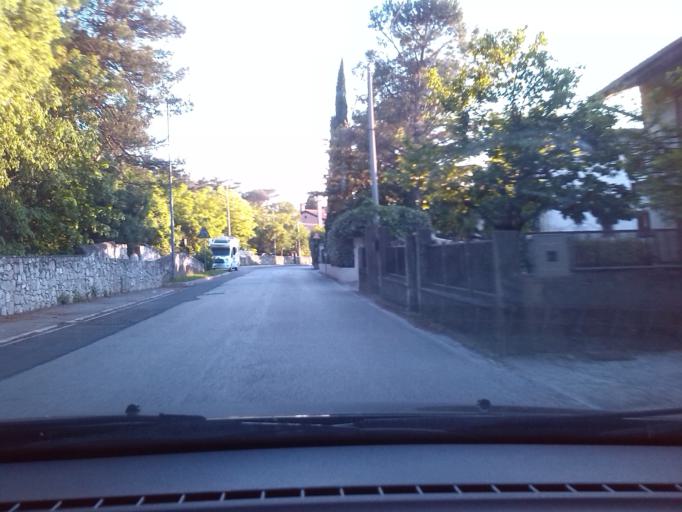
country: IT
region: Friuli Venezia Giulia
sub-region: Provincia di Trieste
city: Duino
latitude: 45.7739
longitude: 13.6083
